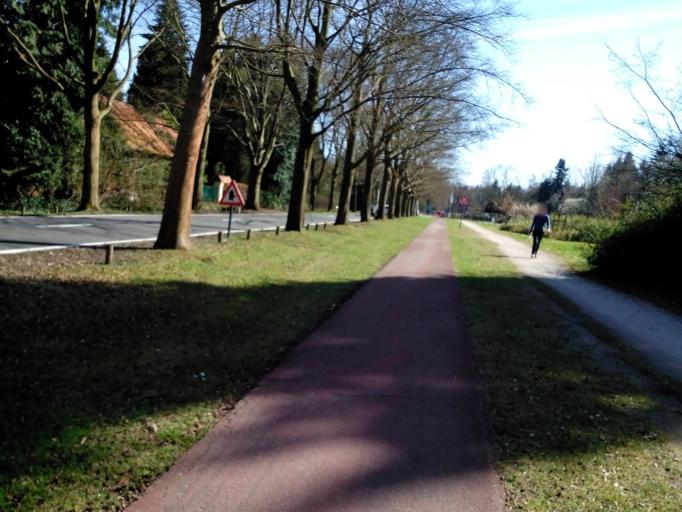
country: BE
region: Flanders
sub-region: Provincie Limburg
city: Diepenbeek
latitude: 50.9571
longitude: 5.4079
